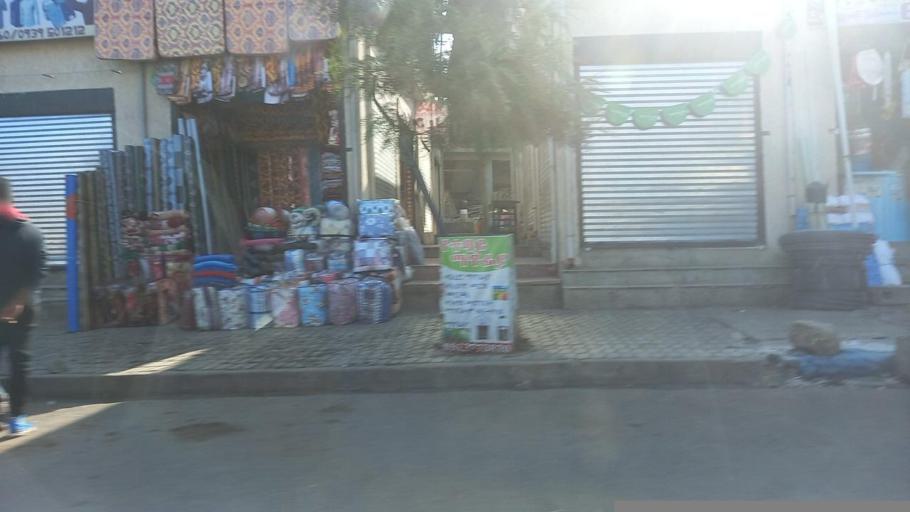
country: ET
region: Adis Abeba
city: Addis Ababa
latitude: 8.9323
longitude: 38.7432
